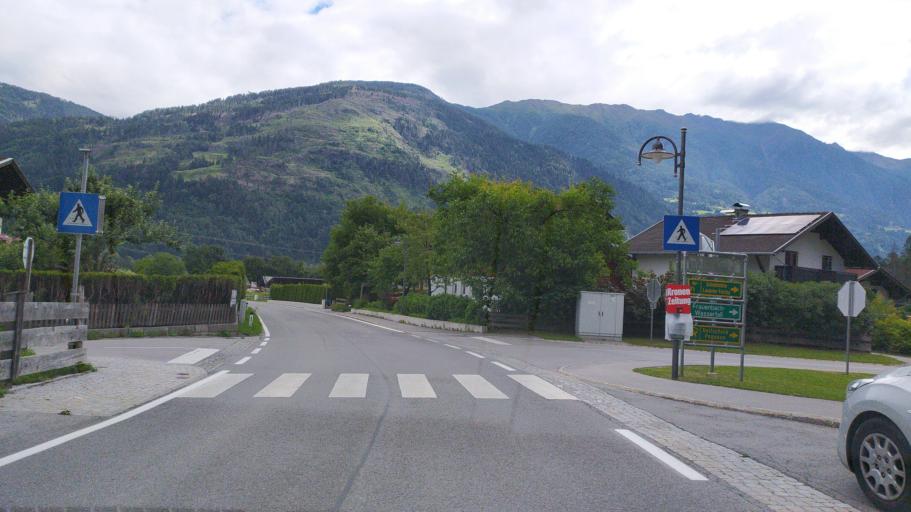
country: AT
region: Tyrol
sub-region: Politischer Bezirk Lienz
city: Lavant
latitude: 46.7975
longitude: 12.8458
